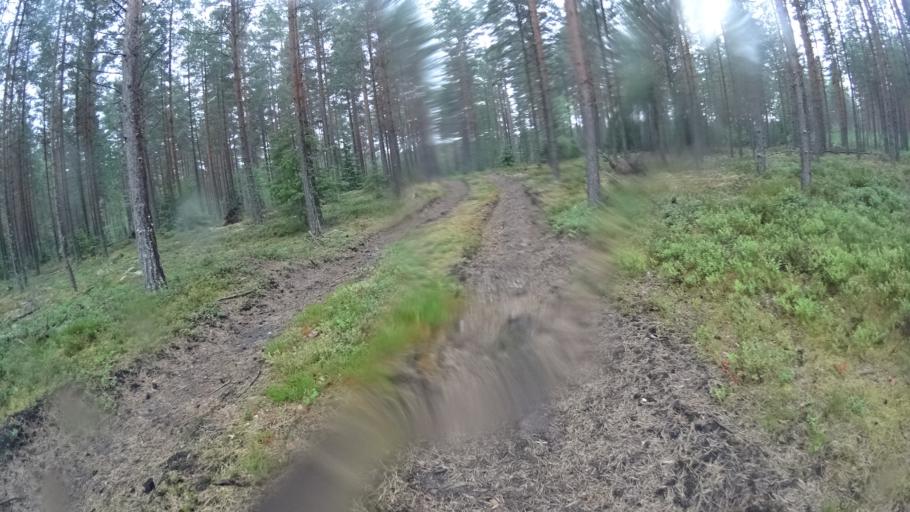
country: FI
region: Uusimaa
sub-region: Helsinki
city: Karkkila
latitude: 60.5917
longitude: 24.1853
